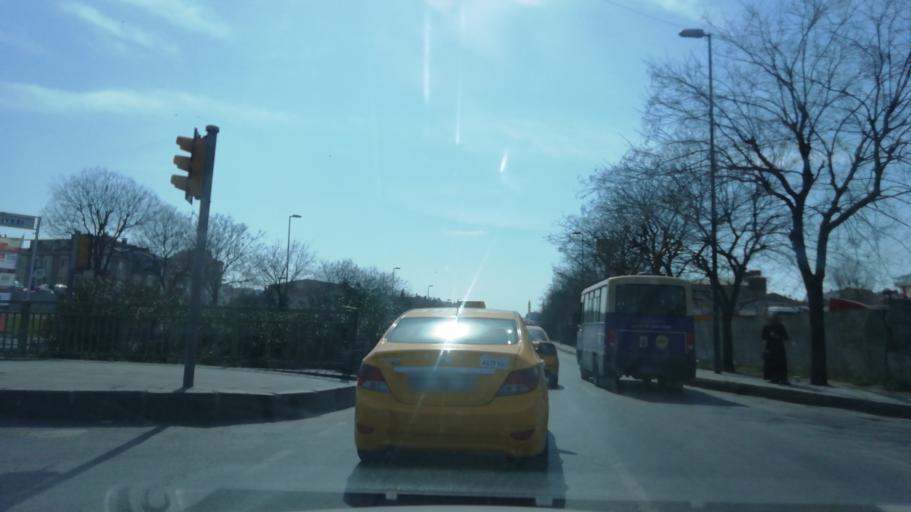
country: TR
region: Istanbul
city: Bagcilar
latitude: 41.0215
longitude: 28.8484
